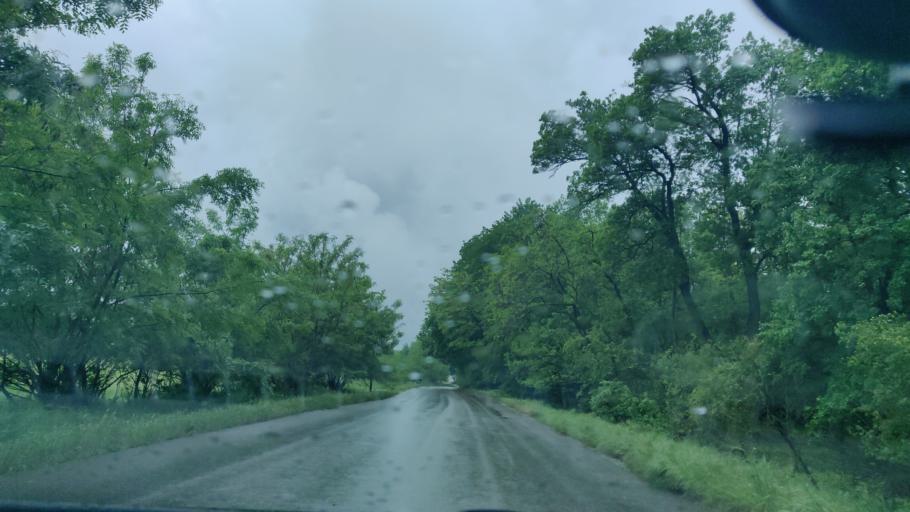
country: RO
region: Giurgiu
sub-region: Comuna Bulbucata
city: Bulbucata
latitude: 44.2871
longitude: 25.7858
